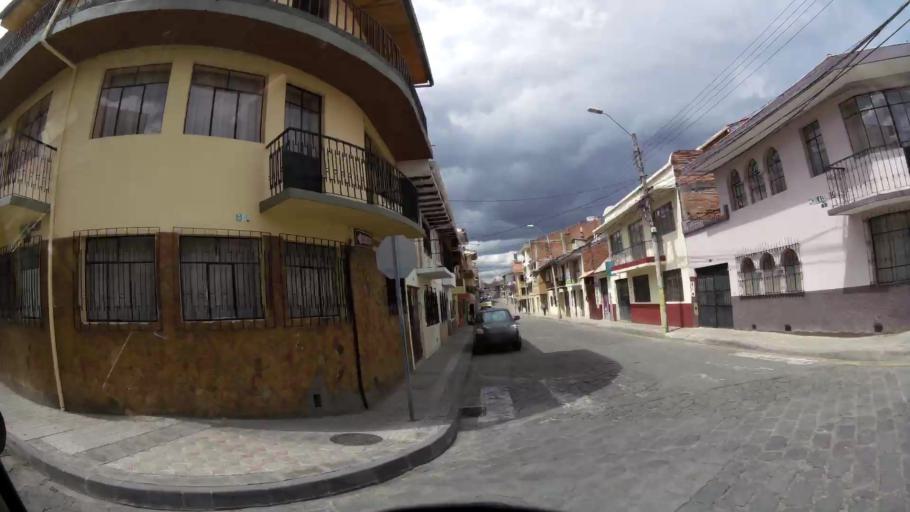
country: EC
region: Azuay
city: Cuenca
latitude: -2.9042
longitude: -78.9983
